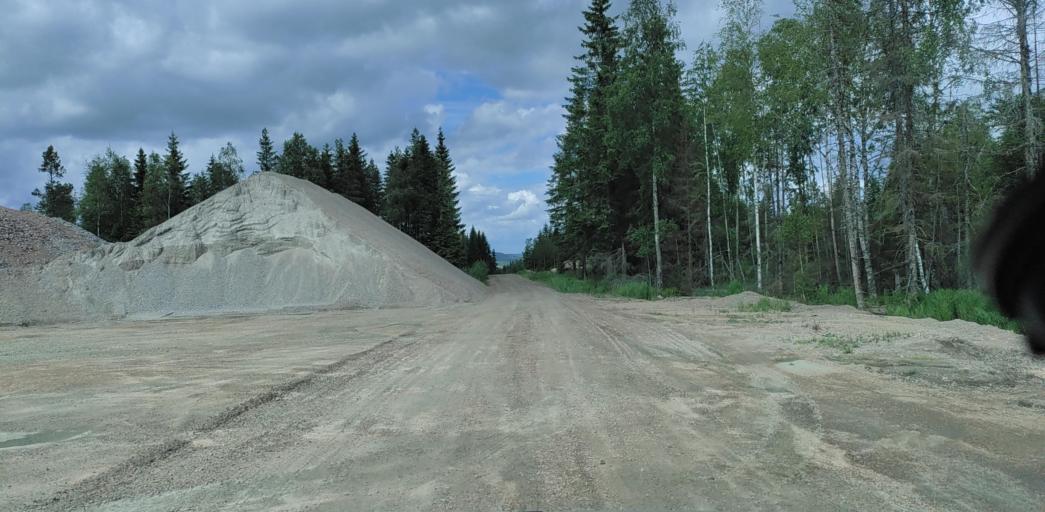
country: SE
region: Vaermland
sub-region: Munkfors Kommun
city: Munkfors
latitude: 59.9549
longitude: 13.4104
